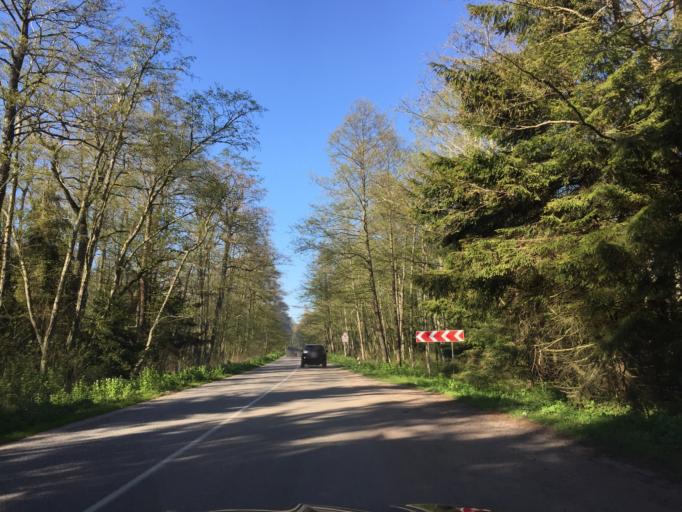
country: LT
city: Nida
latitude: 55.1842
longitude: 20.8549
